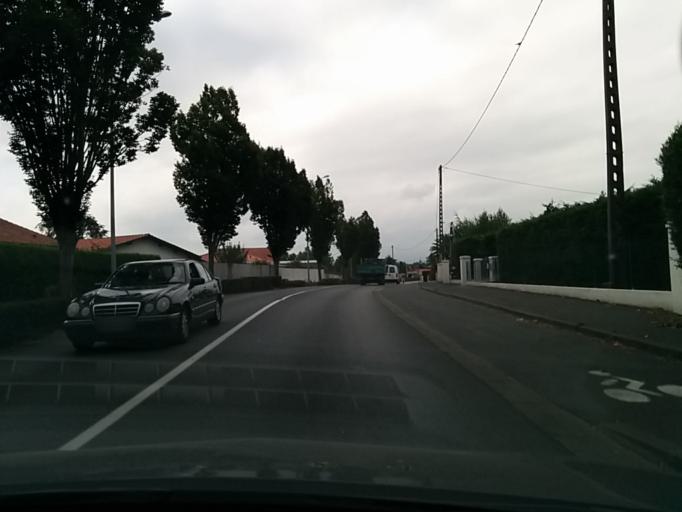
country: FR
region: Aquitaine
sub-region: Departement des Pyrenees-Atlantiques
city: Anglet
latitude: 43.4725
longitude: -1.4991
